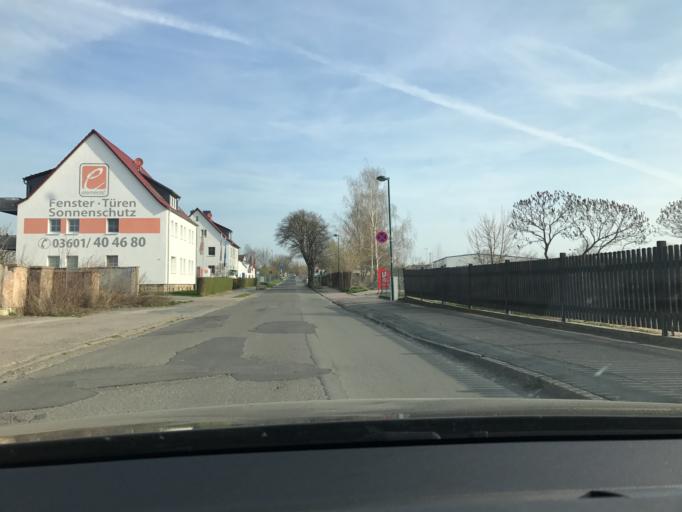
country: DE
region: Thuringia
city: Muehlhausen
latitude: 51.2181
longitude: 10.4597
